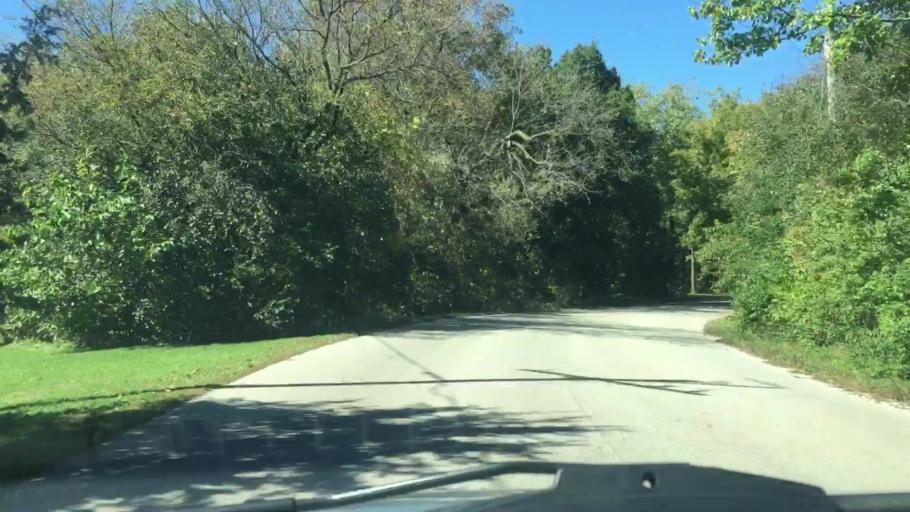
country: US
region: Wisconsin
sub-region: Waukesha County
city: North Prairie
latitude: 42.9303
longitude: -88.4515
